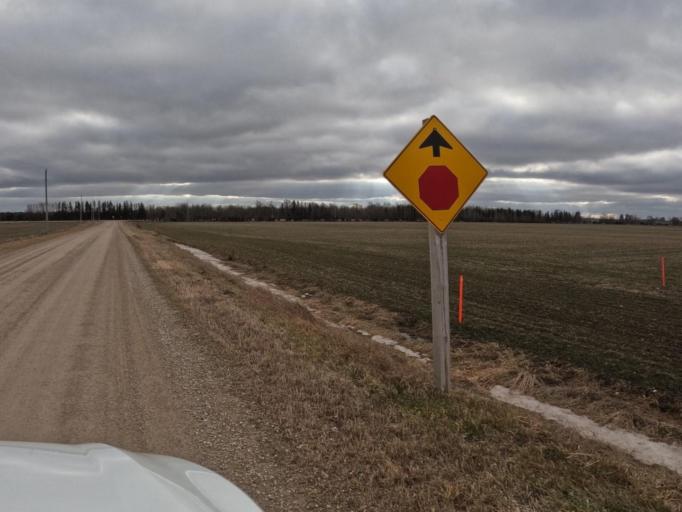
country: CA
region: Ontario
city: Shelburne
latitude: 43.8593
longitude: -80.3994
